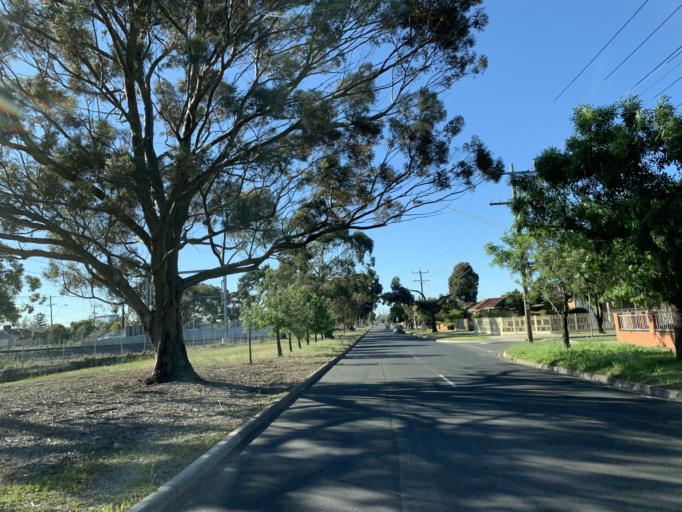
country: AU
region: Victoria
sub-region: Brimbank
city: St Albans
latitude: -37.7539
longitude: 144.8065
